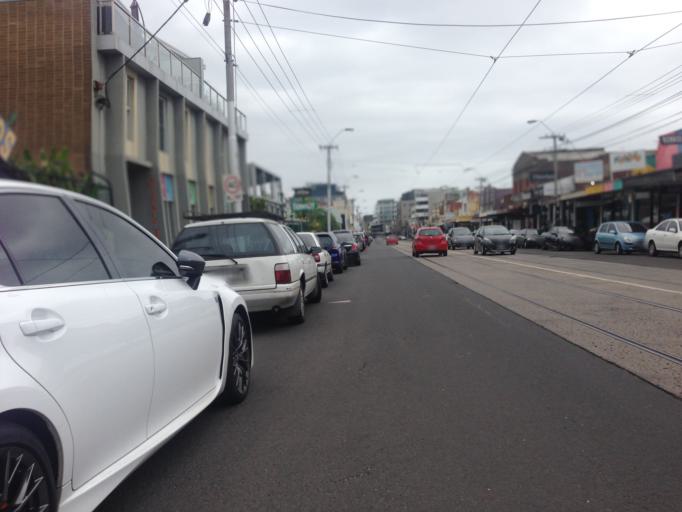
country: AU
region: Victoria
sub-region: Darebin
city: Northcote
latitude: -37.7636
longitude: 144.9998
